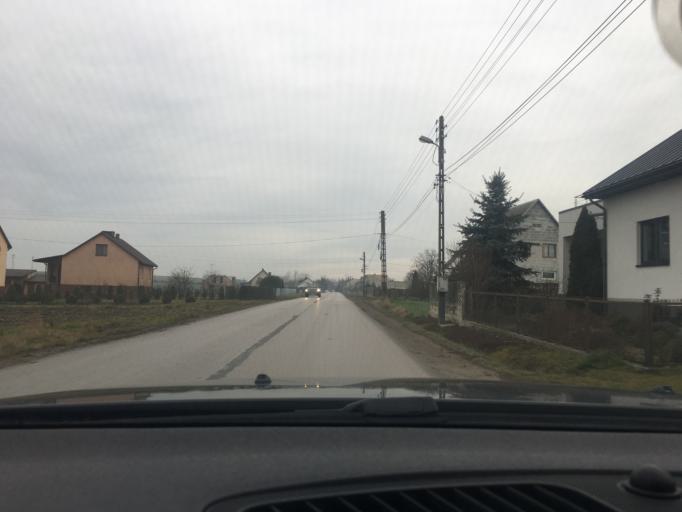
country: PL
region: Swietokrzyskie
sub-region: Powiat jedrzejowski
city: Jedrzejow
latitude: 50.6404
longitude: 20.3672
